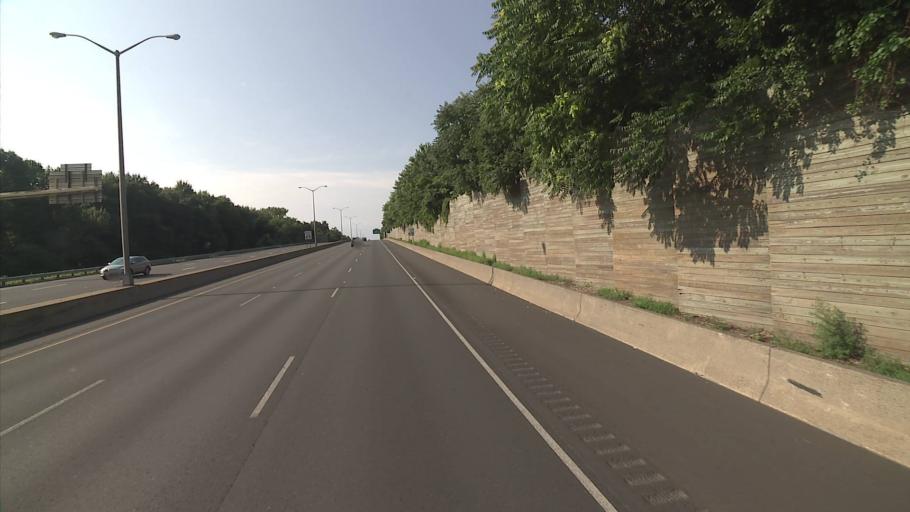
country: US
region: Connecticut
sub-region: Hartford County
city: Thompsonville
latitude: 42.0165
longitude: -72.5870
